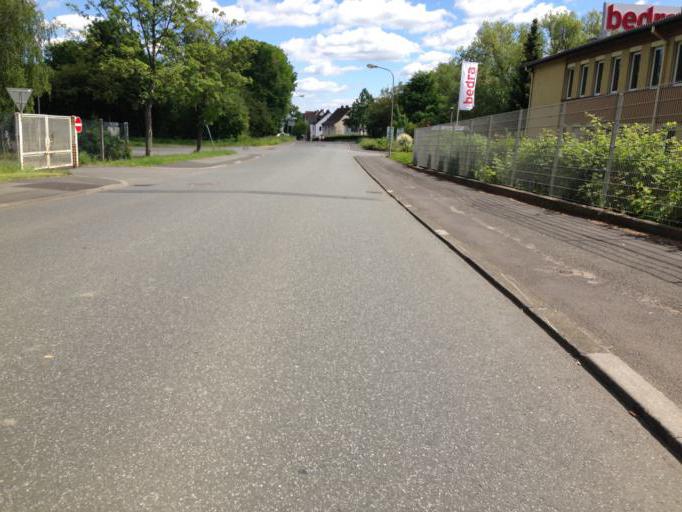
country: DE
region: Hesse
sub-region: Regierungsbezirk Giessen
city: Heuchelheim
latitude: 50.5870
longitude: 8.6194
